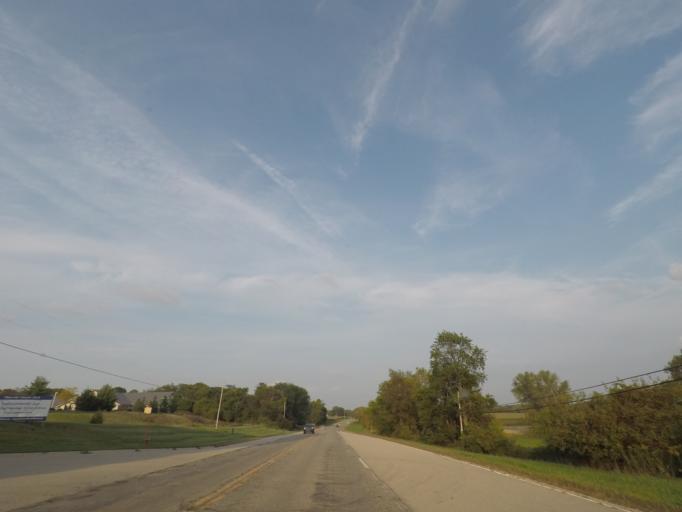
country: US
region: Wisconsin
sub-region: Dane County
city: Cottage Grove
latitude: 43.0874
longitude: -89.2488
